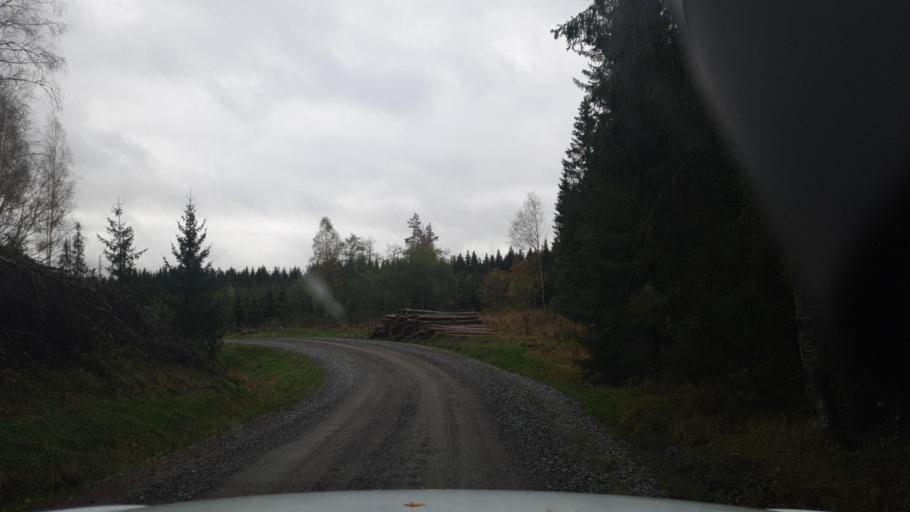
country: SE
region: Vaermland
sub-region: Karlstads Kommun
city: Edsvalla
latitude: 59.4619
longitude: 13.1088
